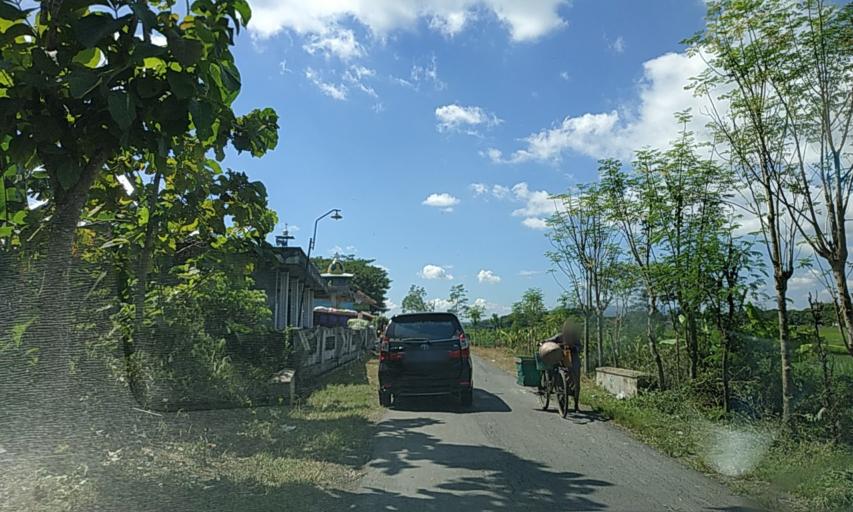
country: ID
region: Central Java
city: Trucuk
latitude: -7.7352
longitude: 110.7212
